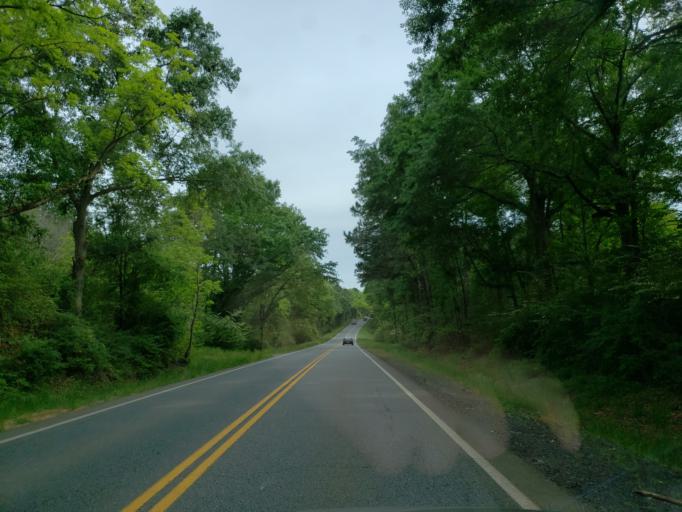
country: US
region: Georgia
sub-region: Macon County
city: Marshallville
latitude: 32.4049
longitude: -83.8659
